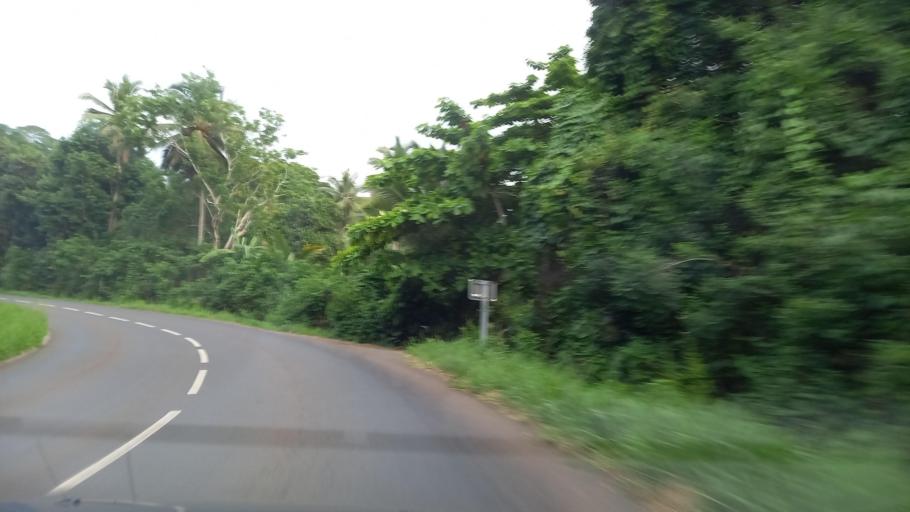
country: YT
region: Tsingoni
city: Tsingoni
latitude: -12.7719
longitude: 45.1036
